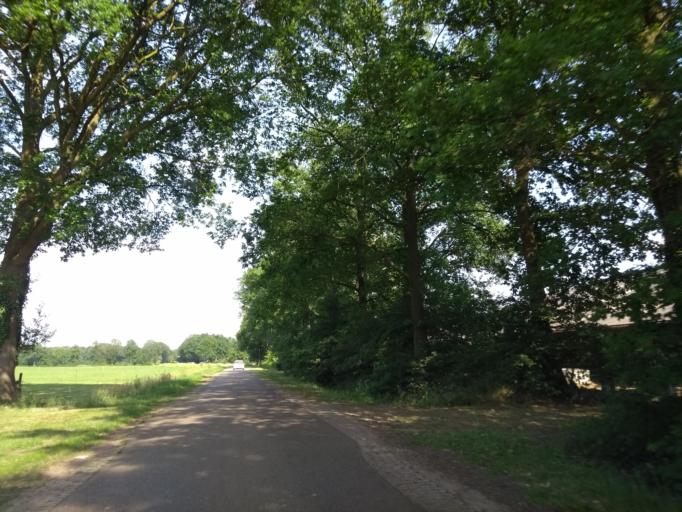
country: DE
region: Lower Saxony
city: Nordhorn
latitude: 52.3693
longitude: 7.0341
